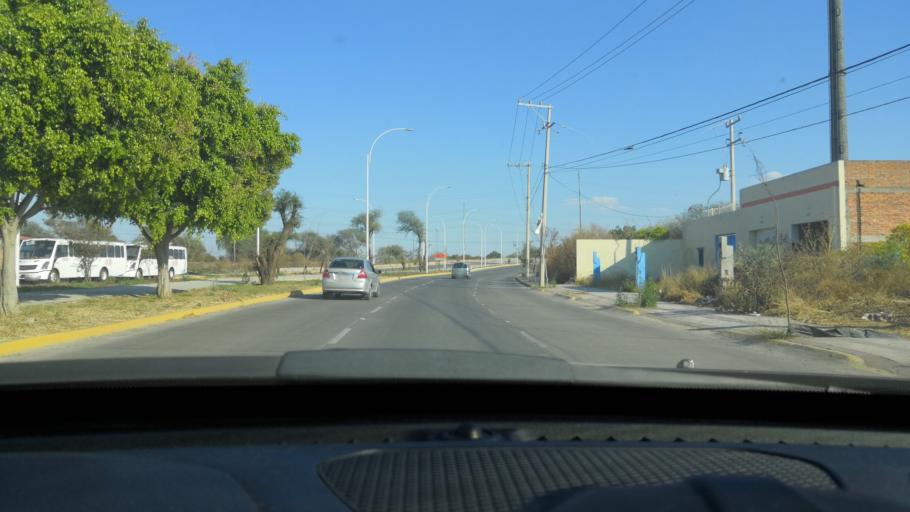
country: MX
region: Guanajuato
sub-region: Leon
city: Fraccionamiento Paraiso Real
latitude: 21.0598
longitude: -101.6111
